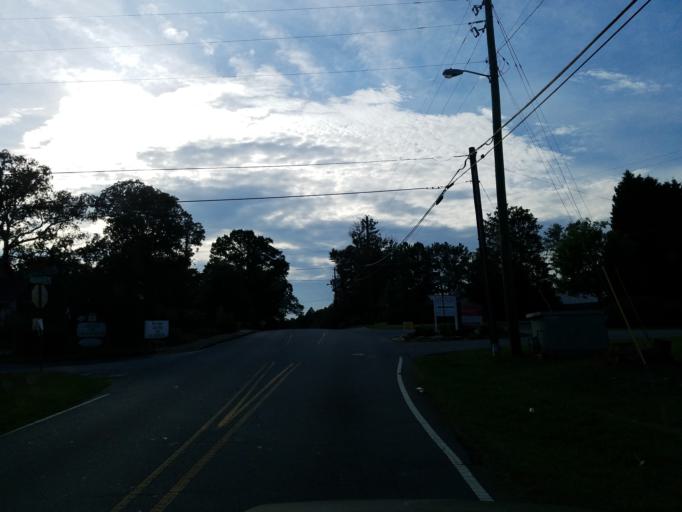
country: US
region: Georgia
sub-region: Cobb County
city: Marietta
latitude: 33.9372
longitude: -84.5513
